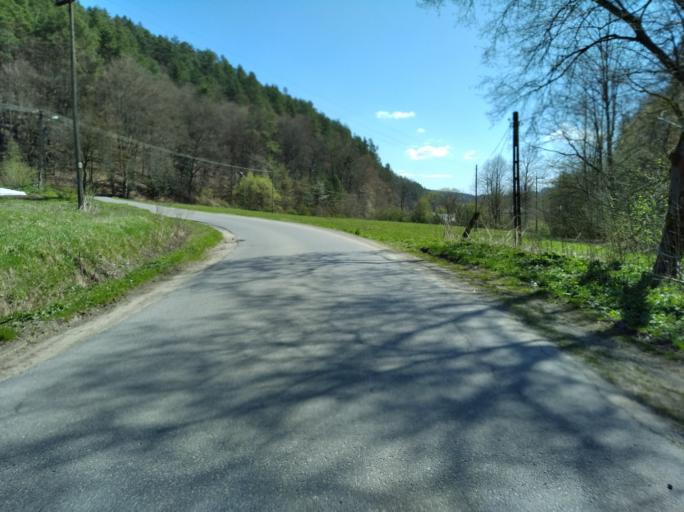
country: PL
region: Subcarpathian Voivodeship
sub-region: Powiat brzozowski
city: Dydnia
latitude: 49.7149
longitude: 22.1888
